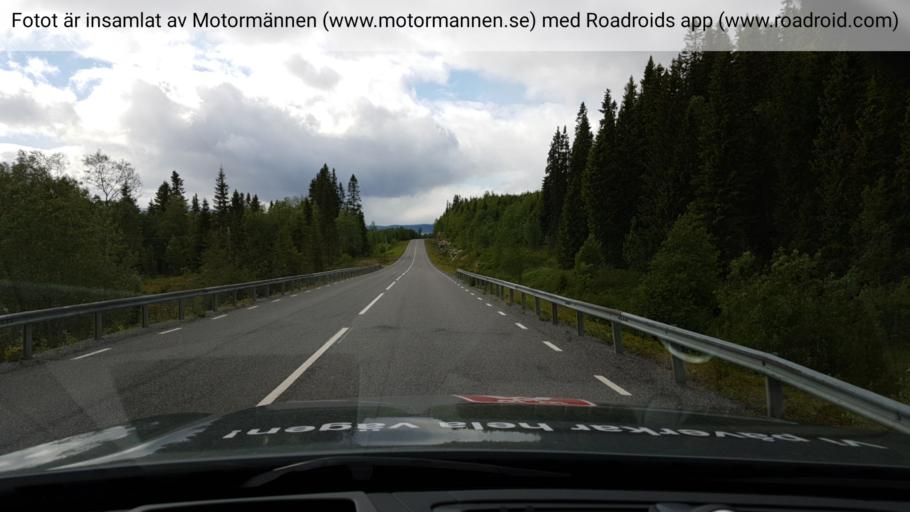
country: SE
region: Jaemtland
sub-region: Are Kommun
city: Are
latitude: 63.6380
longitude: 13.0967
